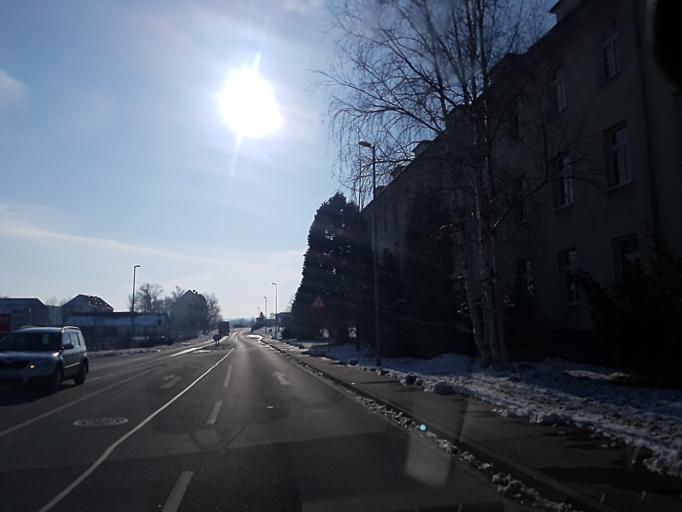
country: DE
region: Saxony
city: Leisnig
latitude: 51.1577
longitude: 12.9150
